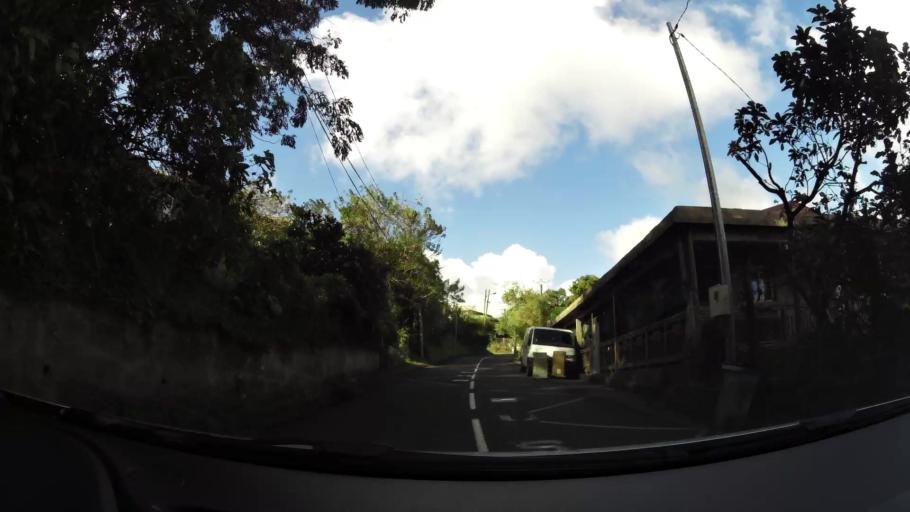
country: MQ
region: Martinique
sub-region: Martinique
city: Saint-Joseph
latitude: 14.6628
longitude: -61.0860
